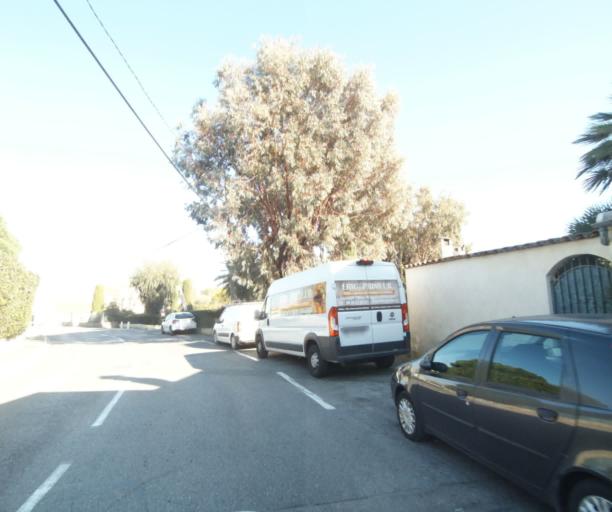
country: FR
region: Provence-Alpes-Cote d'Azur
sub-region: Departement des Alpes-Maritimes
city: Biot
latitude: 43.6038
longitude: 7.1167
